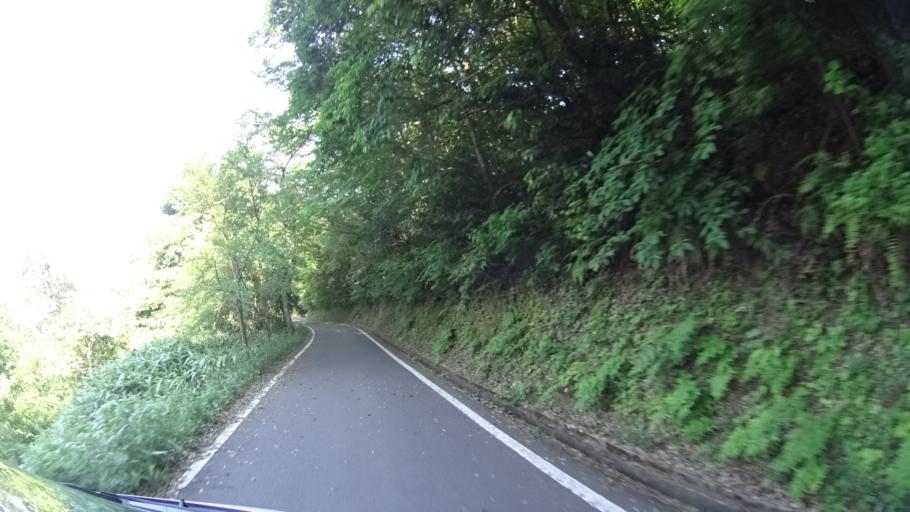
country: JP
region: Kyoto
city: Miyazu
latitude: 35.5662
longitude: 135.1420
